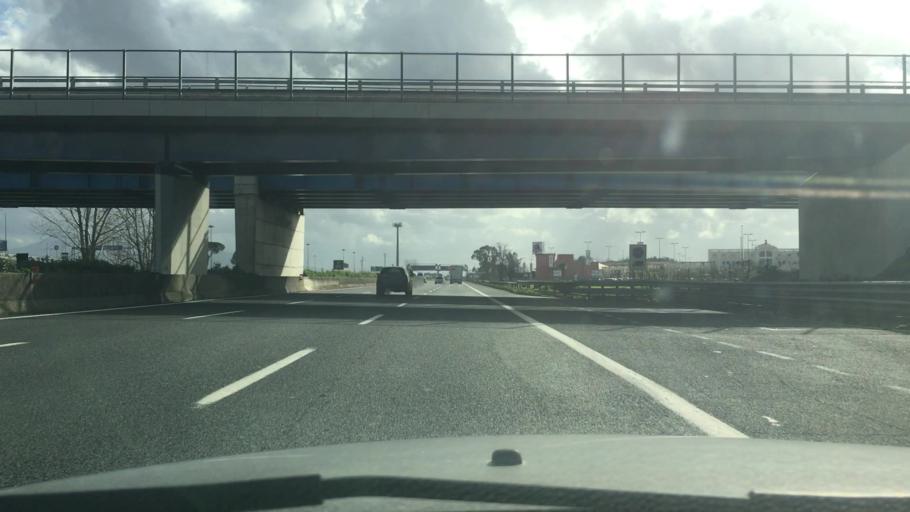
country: IT
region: Campania
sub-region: Provincia di Caserta
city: San Marco Evangelista
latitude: 41.0109
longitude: 14.3228
